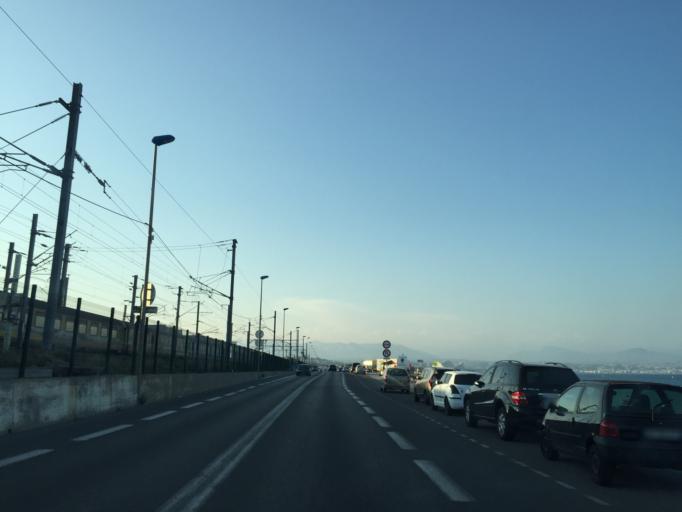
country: FR
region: Provence-Alpes-Cote d'Azur
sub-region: Departement des Alpes-Maritimes
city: Antibes
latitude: 43.5984
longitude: 7.1254
